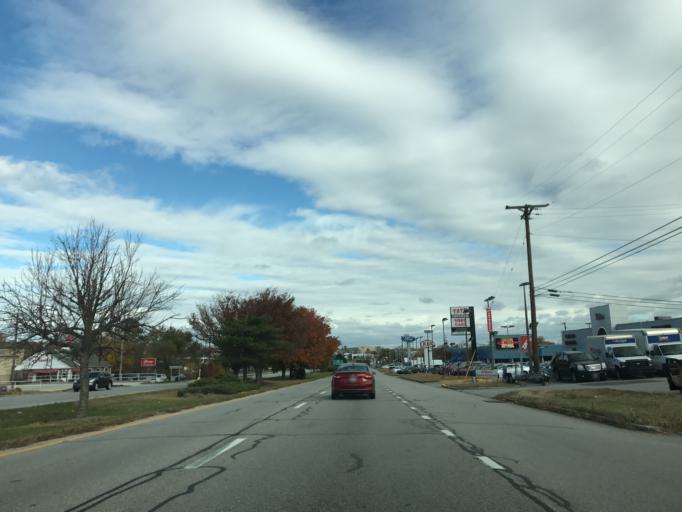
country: US
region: Maryland
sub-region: Anne Arundel County
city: Glen Burnie
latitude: 39.1779
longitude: -76.6157
